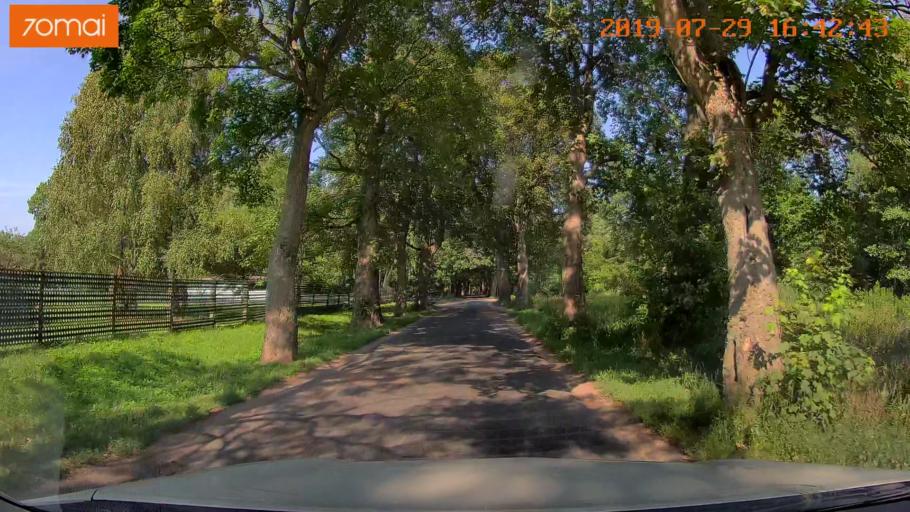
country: RU
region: Kaliningrad
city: Primorsk
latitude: 54.7446
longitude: 20.0763
